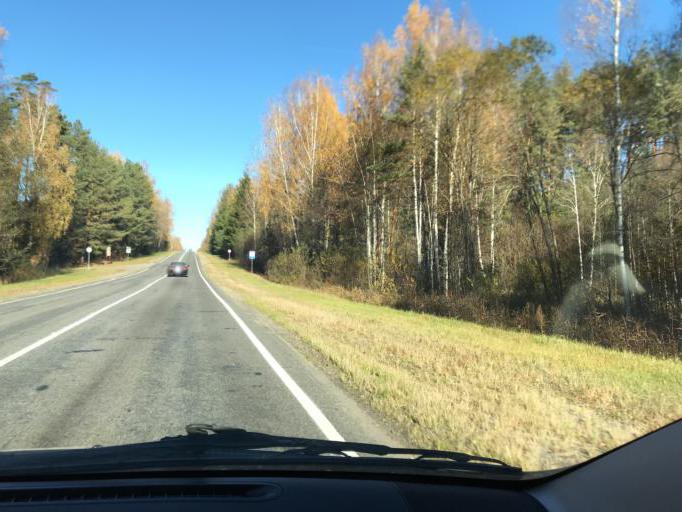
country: BY
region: Vitebsk
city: Lyepyel'
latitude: 54.9797
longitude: 28.7444
